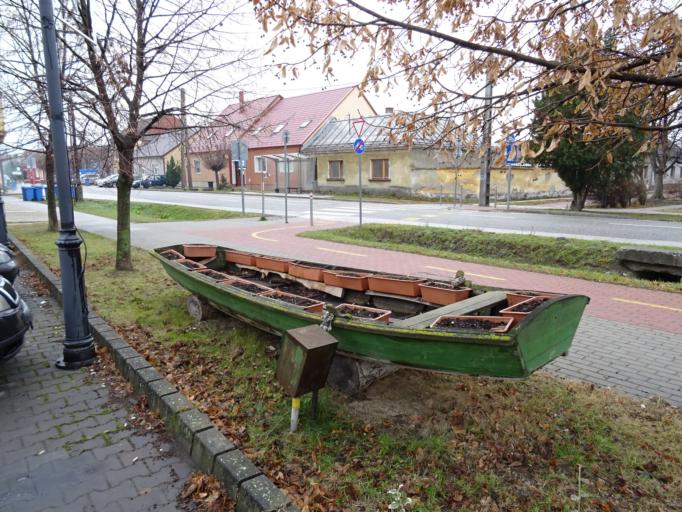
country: HU
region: Gyor-Moson-Sopron
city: Rajka
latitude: 47.9984
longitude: 17.2002
